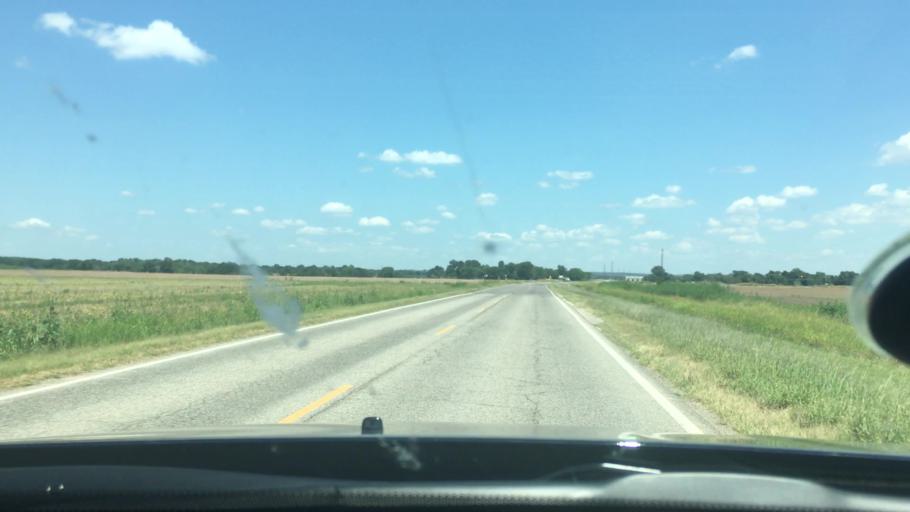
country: US
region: Oklahoma
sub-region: Carter County
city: Dickson
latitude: 34.2234
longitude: -96.9771
